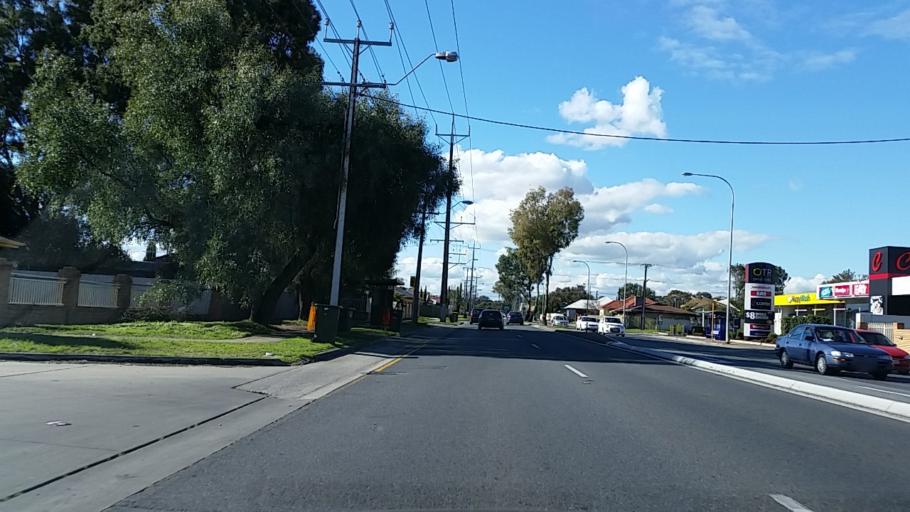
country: AU
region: South Australia
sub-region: Salisbury
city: Salisbury
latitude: -34.7673
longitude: 138.6370
